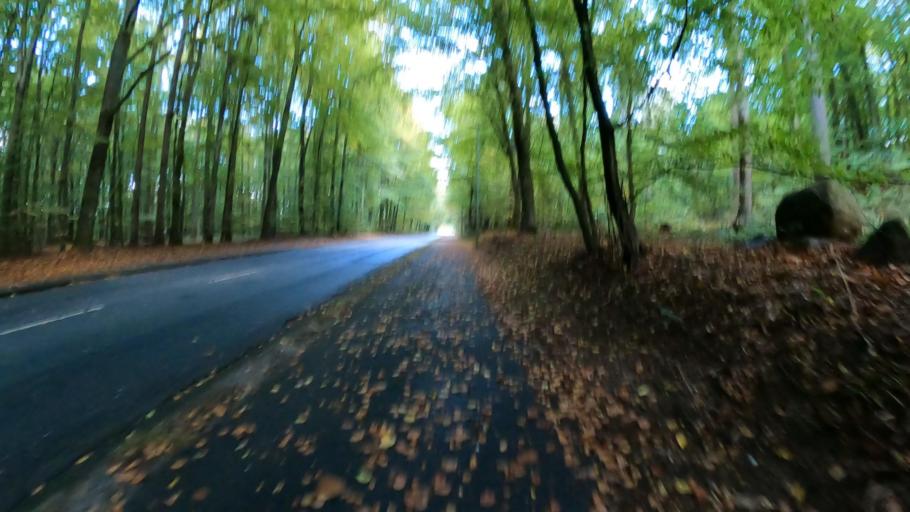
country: DE
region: Schleswig-Holstein
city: Ahrensburg
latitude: 53.6521
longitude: 10.2304
